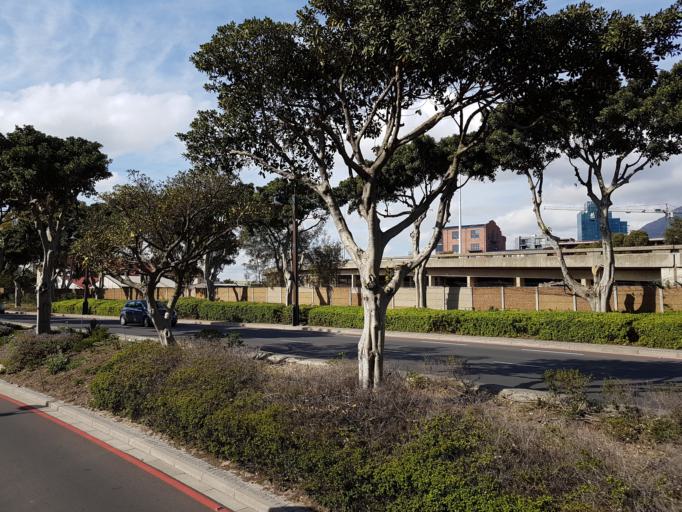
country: ZA
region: Western Cape
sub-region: City of Cape Town
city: Cape Town
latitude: -33.9110
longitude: 18.4174
